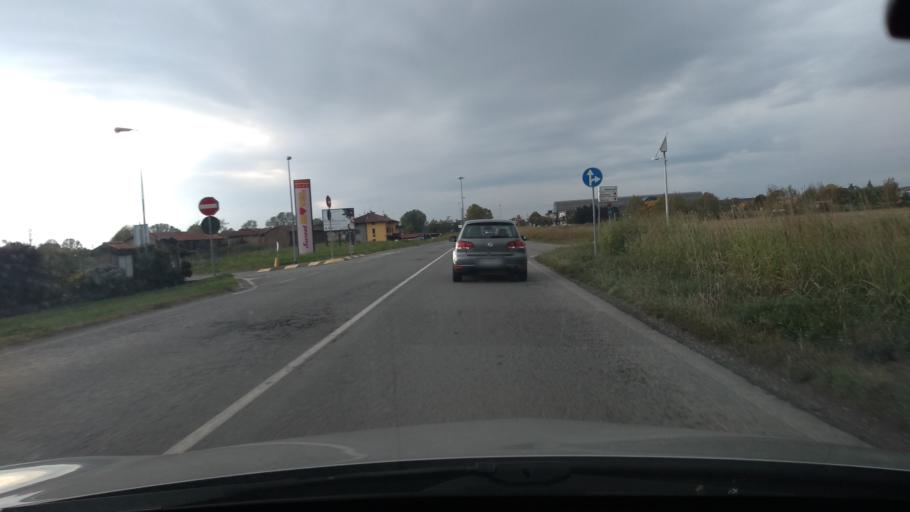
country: IT
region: Lombardy
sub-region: Provincia di Bergamo
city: Pognano
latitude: 45.5911
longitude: 9.6302
